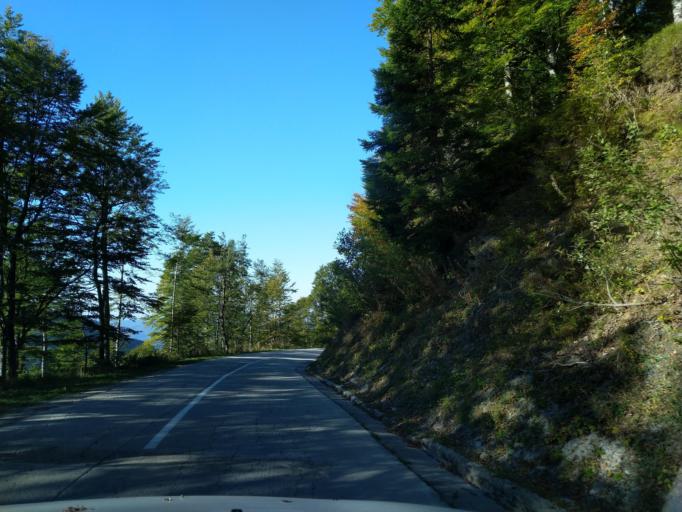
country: RS
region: Central Serbia
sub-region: Moravicki Okrug
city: Ivanjica
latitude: 43.4349
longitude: 20.2677
